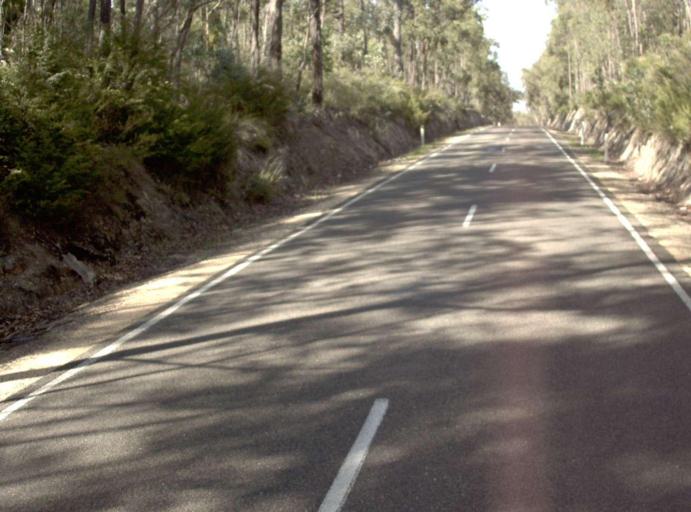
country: AU
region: Victoria
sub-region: East Gippsland
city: Lakes Entrance
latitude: -37.6565
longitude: 148.0914
